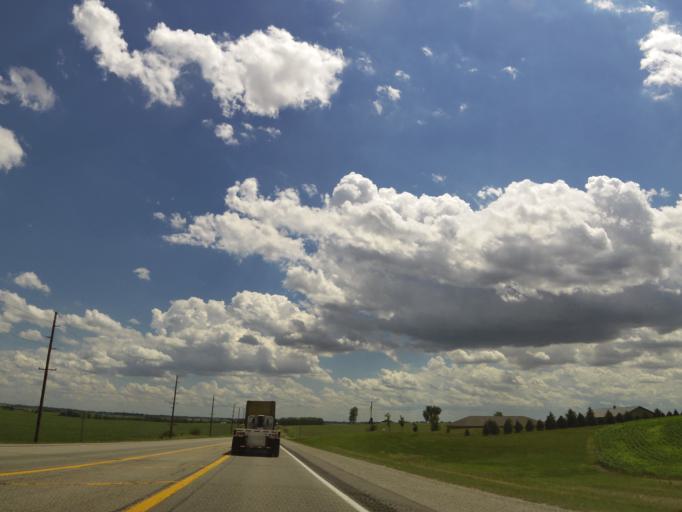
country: US
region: Iowa
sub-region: Benton County
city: Urbana
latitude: 42.2826
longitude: -91.8900
